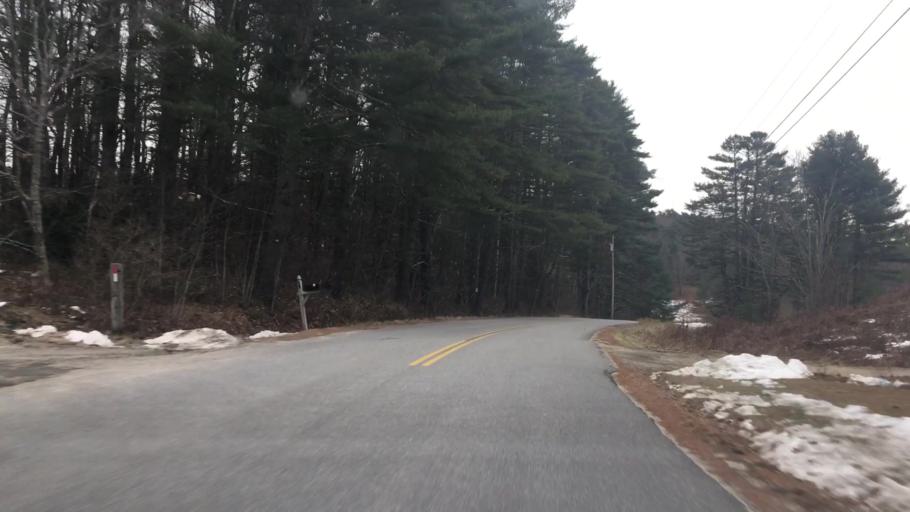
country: US
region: Maine
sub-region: Cumberland County
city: Freeport
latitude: 43.8598
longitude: -70.0857
